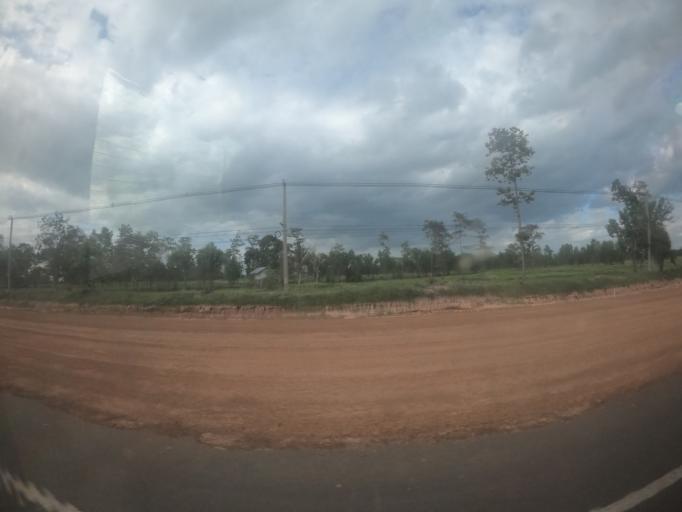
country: TH
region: Surin
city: Kap Choeng
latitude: 14.5121
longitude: 103.5510
